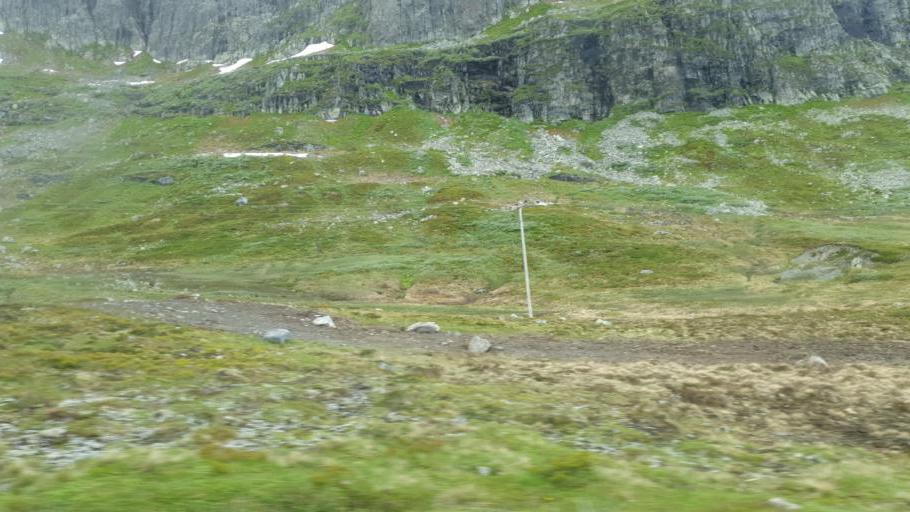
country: NO
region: Oppland
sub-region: Vestre Slidre
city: Slidre
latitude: 61.3020
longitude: 8.8079
